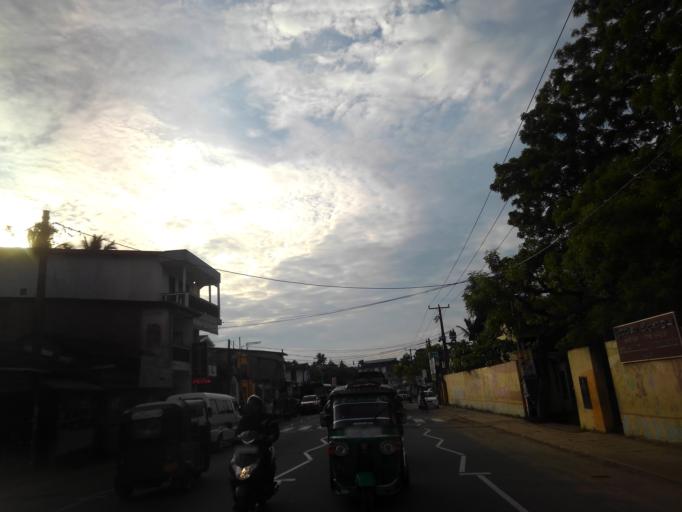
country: LK
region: Southern
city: Unawatuna
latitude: 6.0337
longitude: 80.2371
